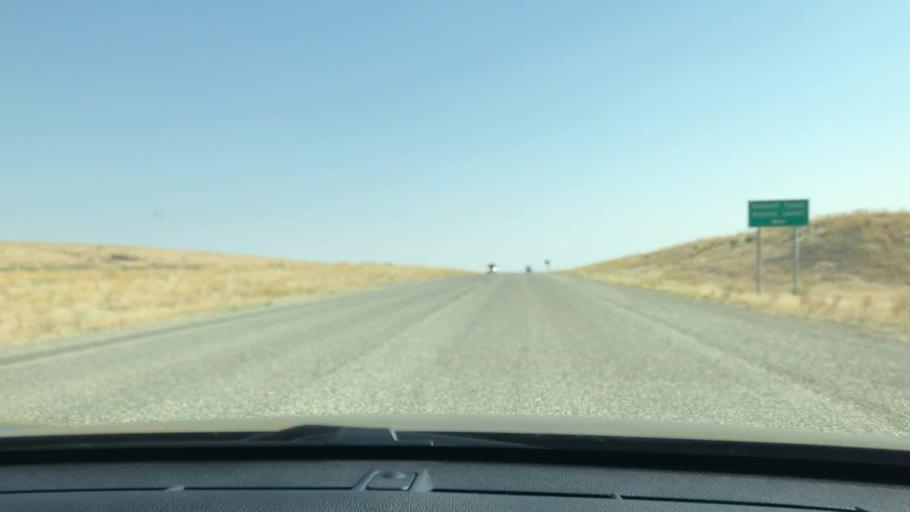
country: US
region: Nevada
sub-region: Humboldt County
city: Winnemucca
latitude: 41.0222
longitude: -117.7263
